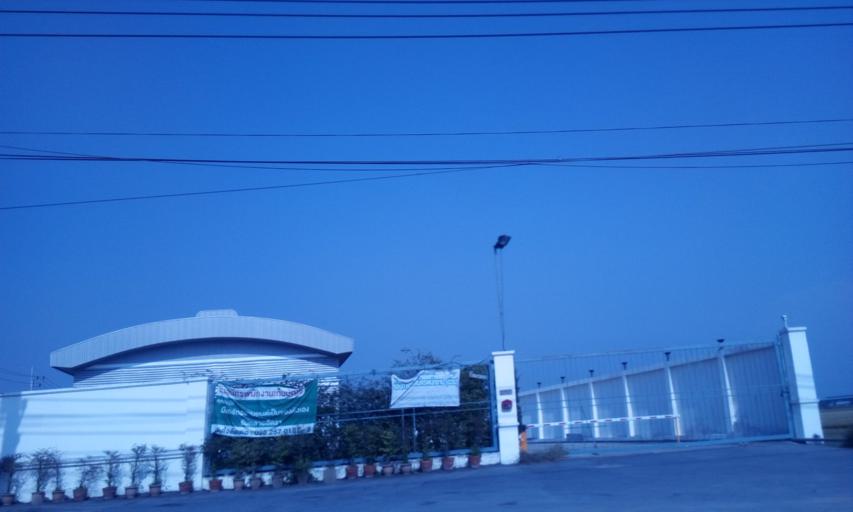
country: TH
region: Nonthaburi
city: Sai Noi
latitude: 14.0392
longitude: 100.3122
